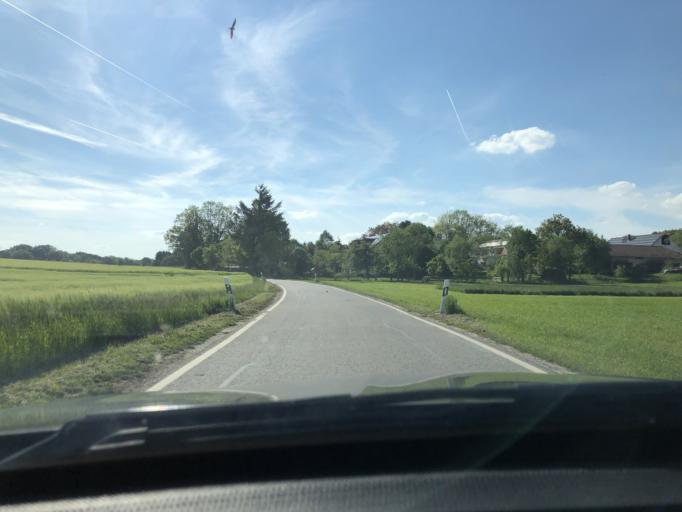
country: DE
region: Bavaria
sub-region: Upper Bavaria
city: Zolling
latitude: 48.4361
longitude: 11.7378
